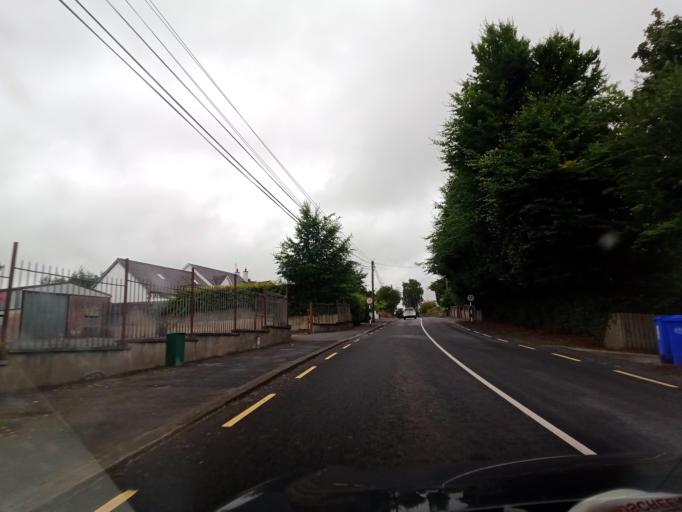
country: IE
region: Leinster
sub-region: Laois
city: Abbeyleix
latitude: 52.9105
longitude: -7.3279
